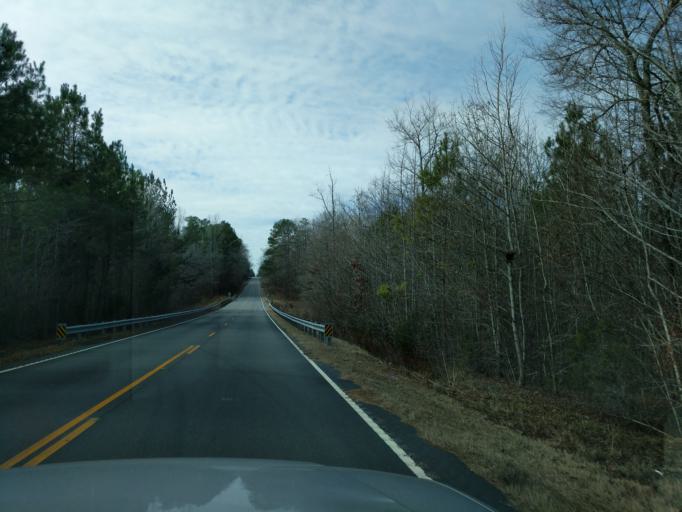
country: US
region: South Carolina
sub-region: Edgefield County
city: Edgefield
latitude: 33.9332
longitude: -81.9771
